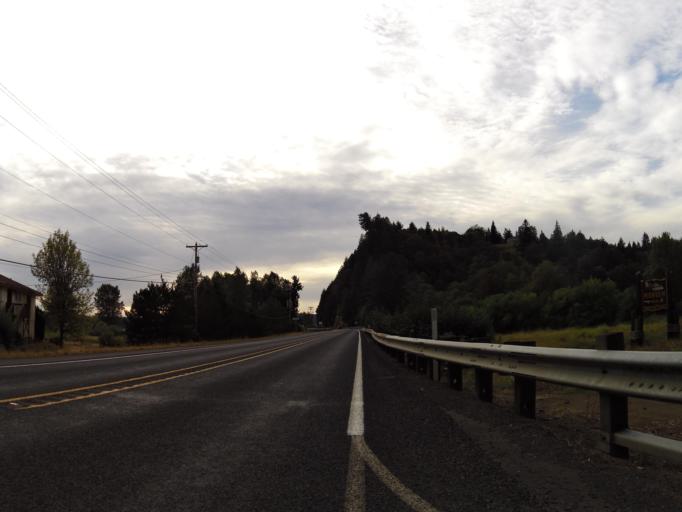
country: US
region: Oregon
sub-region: Columbia County
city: Clatskanie
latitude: 46.1901
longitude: -123.1212
